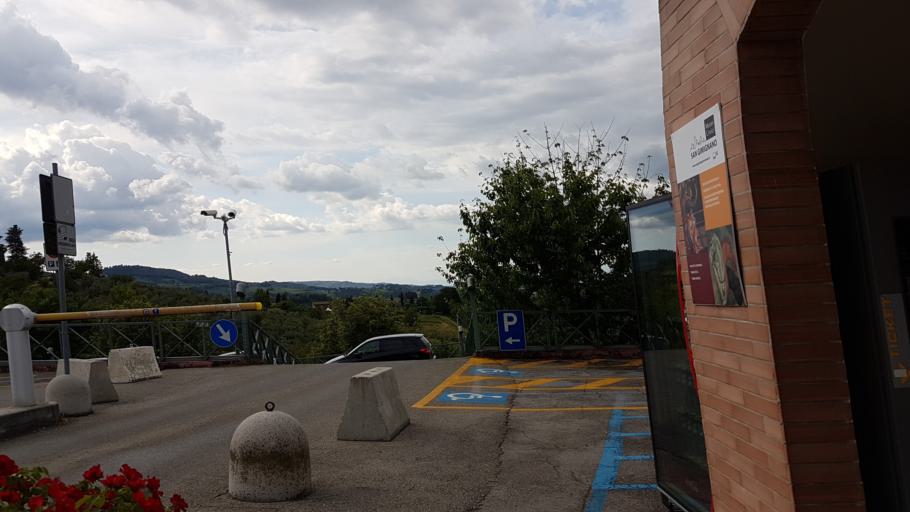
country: IT
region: Tuscany
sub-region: Provincia di Siena
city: San Gimignano
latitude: 43.4710
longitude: 11.0449
